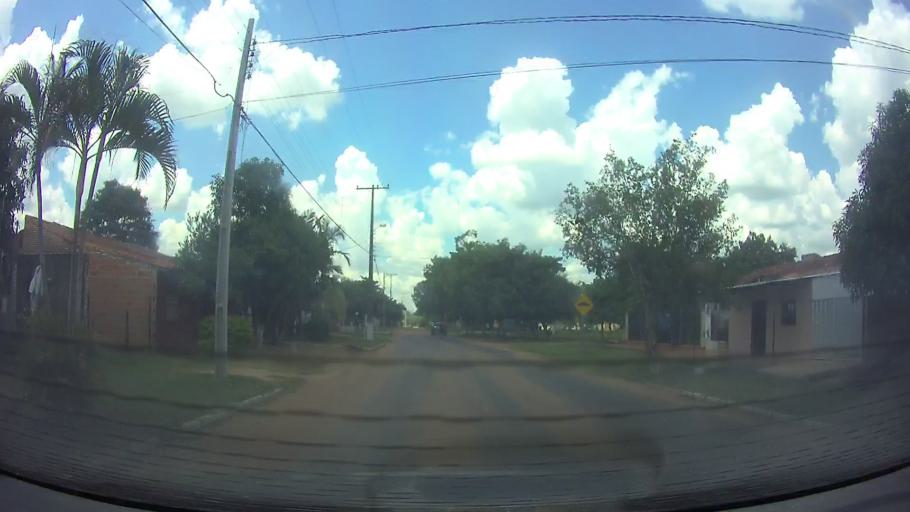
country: PY
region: Central
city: Limpio
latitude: -25.1650
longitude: -57.4305
